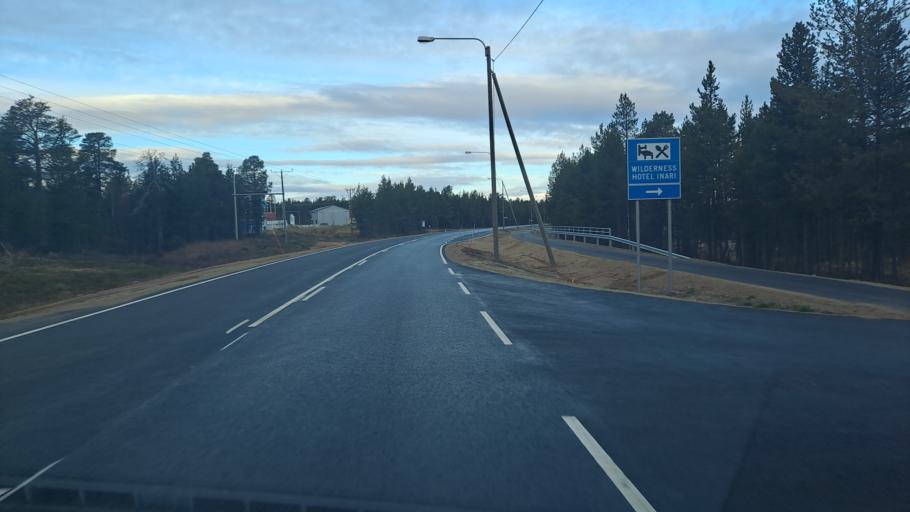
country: FI
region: Lapland
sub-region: Pohjois-Lappi
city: Inari
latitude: 68.8978
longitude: 27.0851
